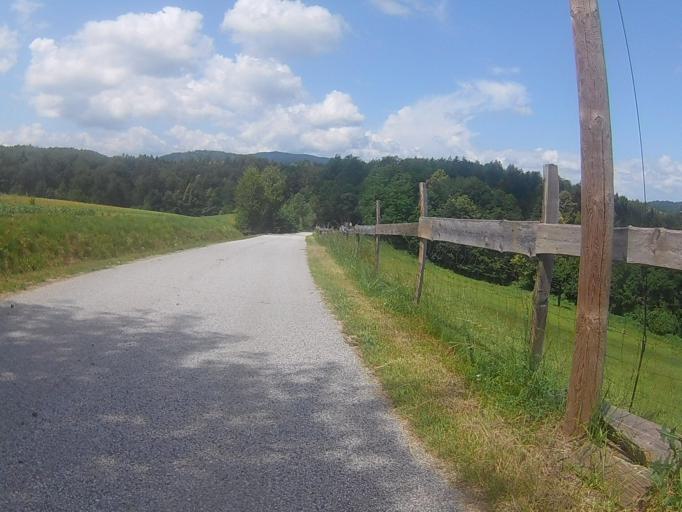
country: SI
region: Kungota
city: Zgornja Kungota
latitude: 46.6137
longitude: 15.5928
